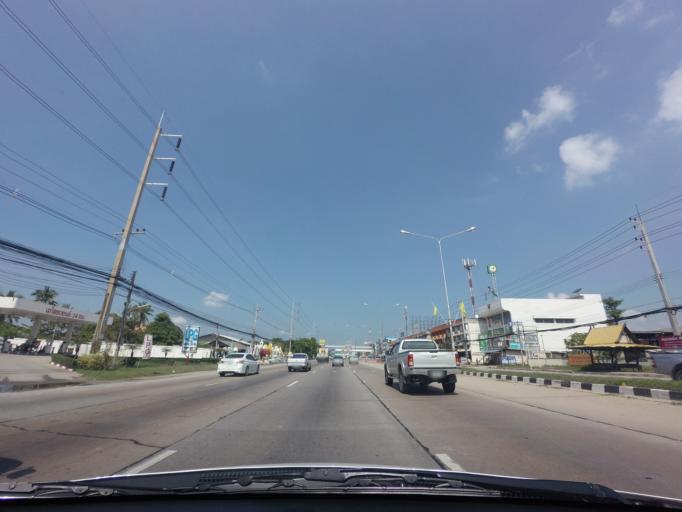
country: TH
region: Nakhon Pathom
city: Nakhon Chai Si
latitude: 13.7830
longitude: 100.1749
